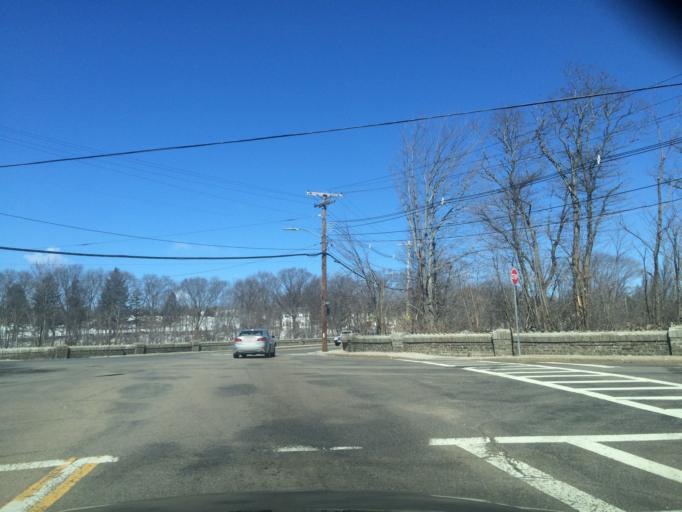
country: US
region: Massachusetts
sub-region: Norfolk County
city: Dedham
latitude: 42.2448
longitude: -71.1358
